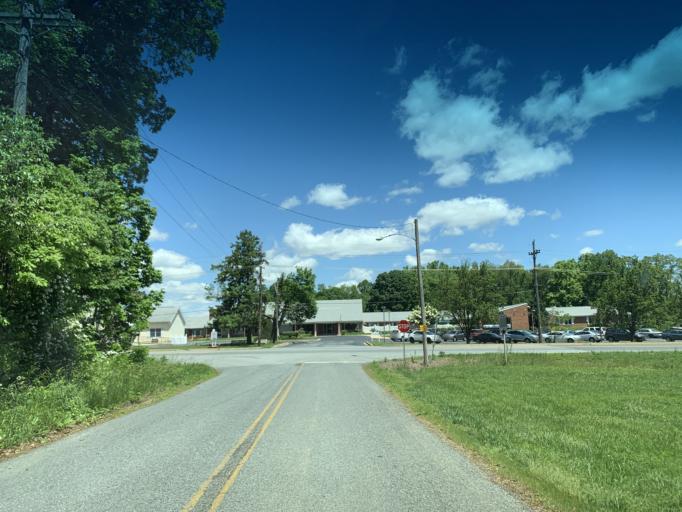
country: US
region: Maryland
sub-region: Cecil County
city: Rising Sun
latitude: 39.7025
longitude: -75.9811
